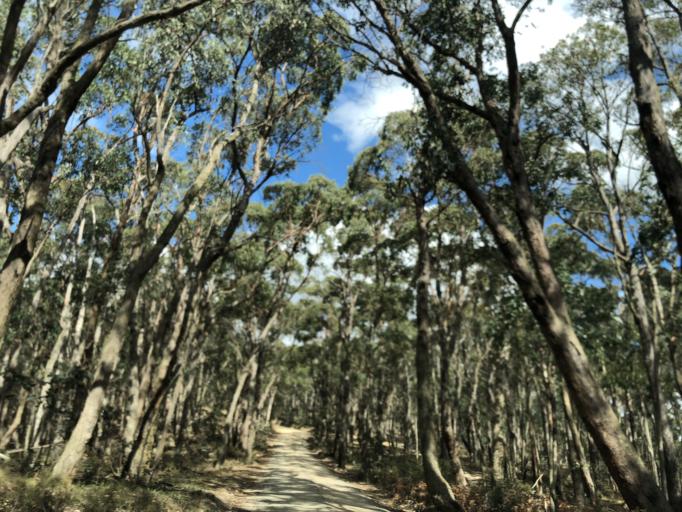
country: AU
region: Victoria
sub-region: Moorabool
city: Bacchus Marsh
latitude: -37.5511
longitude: 144.3466
